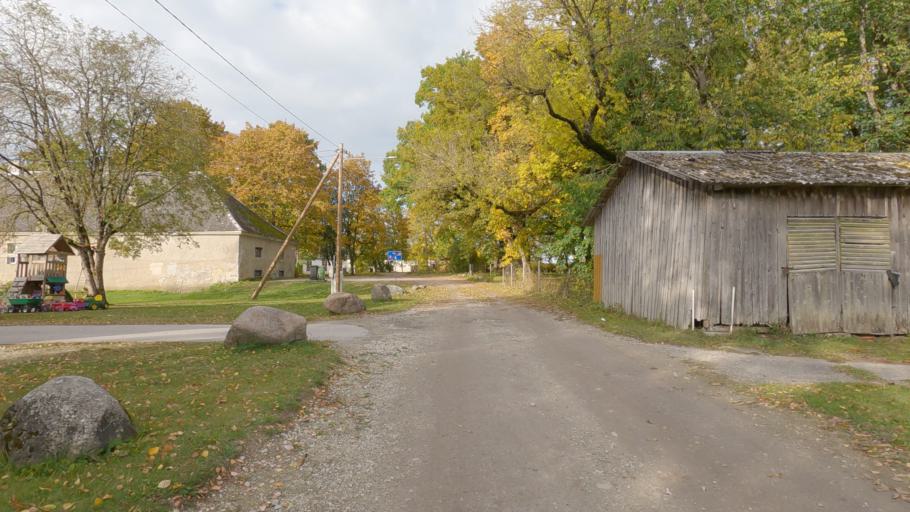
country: EE
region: Raplamaa
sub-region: Rapla vald
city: Rapla
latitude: 58.9346
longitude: 24.7555
